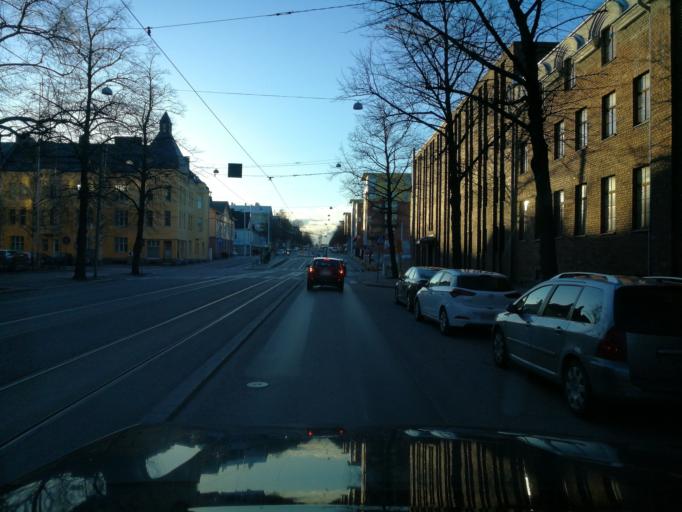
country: FI
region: Uusimaa
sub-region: Helsinki
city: Helsinki
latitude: 60.1924
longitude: 24.9452
